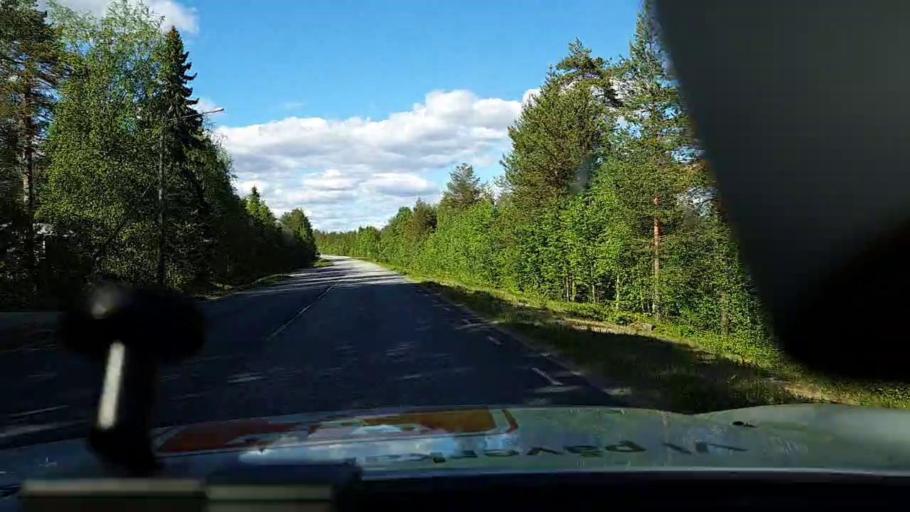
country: FI
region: Lapland
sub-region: Torniolaakso
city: Ylitornio
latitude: 66.3399
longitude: 23.6459
